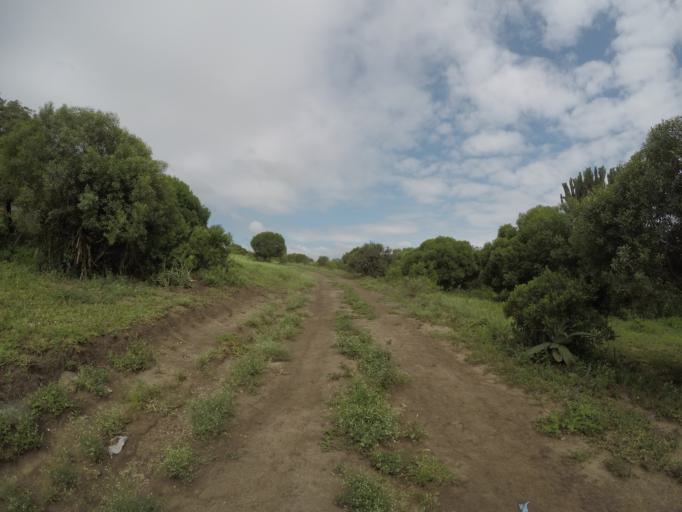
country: ZA
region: KwaZulu-Natal
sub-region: uThungulu District Municipality
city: Empangeni
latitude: -28.6249
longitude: 31.8642
